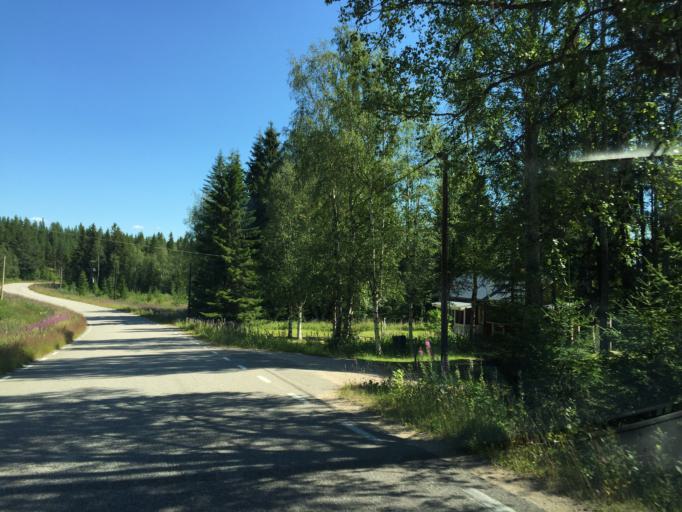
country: SE
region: Gaevleborg
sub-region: Ljusdals Kommun
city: Farila
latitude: 61.7476
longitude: 15.1212
